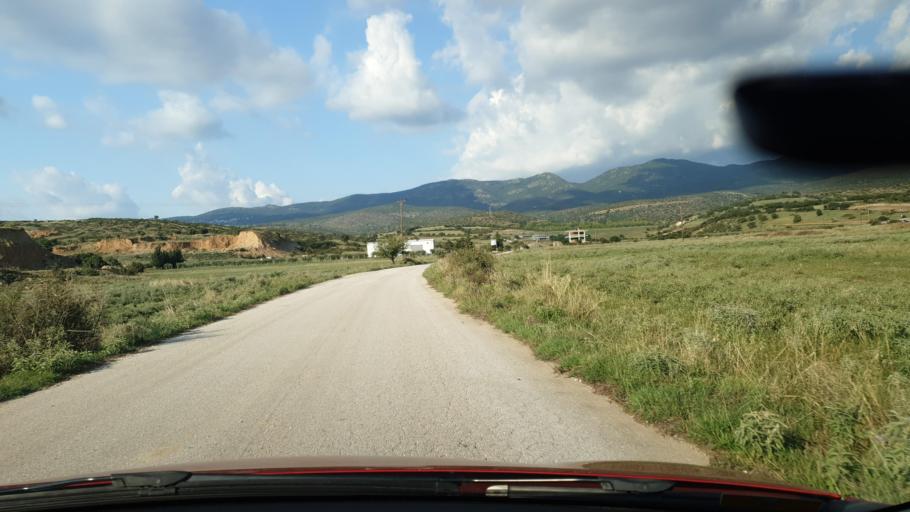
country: GR
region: Central Macedonia
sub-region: Nomos Thessalonikis
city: Vasilika
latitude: 40.4992
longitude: 23.1430
